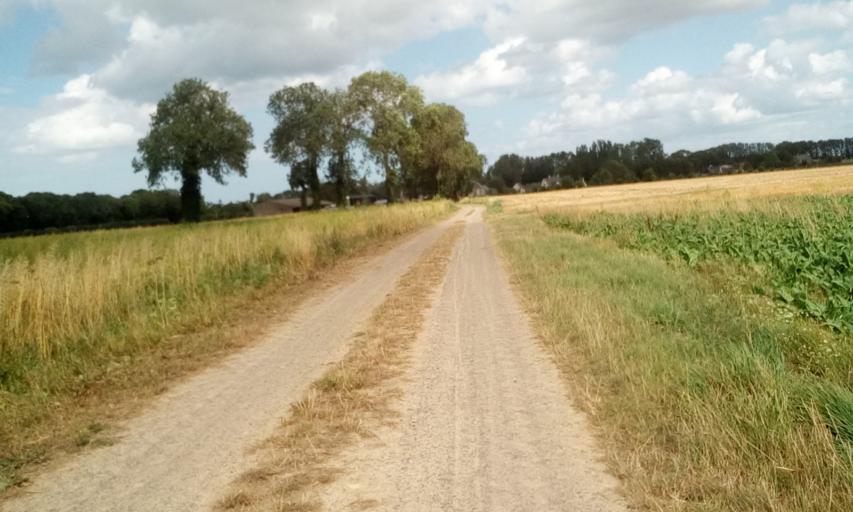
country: FR
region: Lower Normandy
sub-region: Departement du Calvados
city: Creully
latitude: 49.3094
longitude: -0.5576
